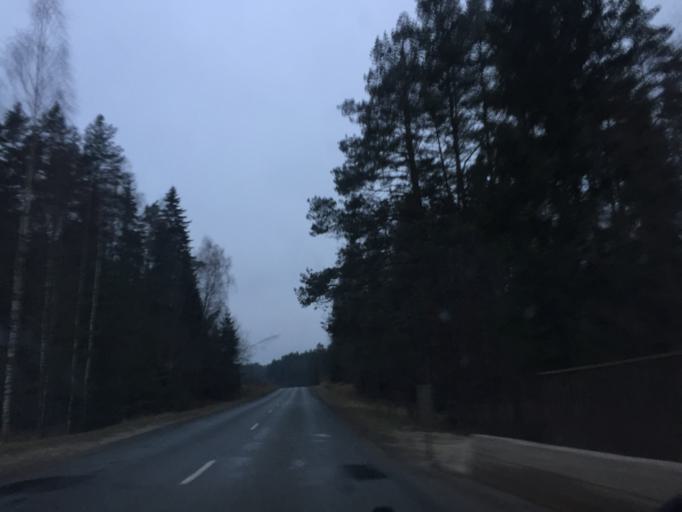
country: LV
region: Priekuli
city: Priekuli
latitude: 57.3286
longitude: 25.4059
